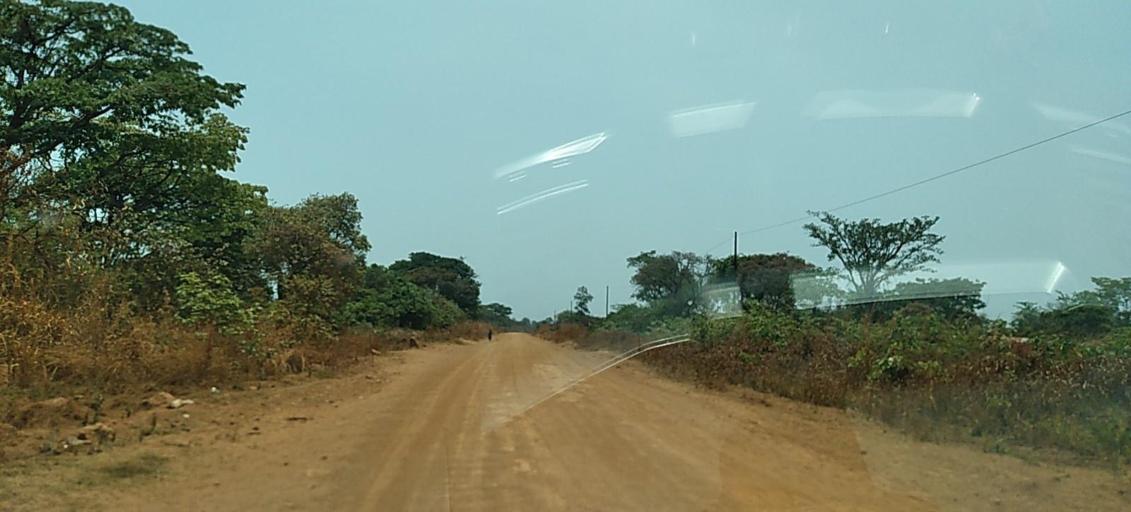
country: CD
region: Katanga
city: Kipushi
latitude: -11.9333
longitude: 26.9734
